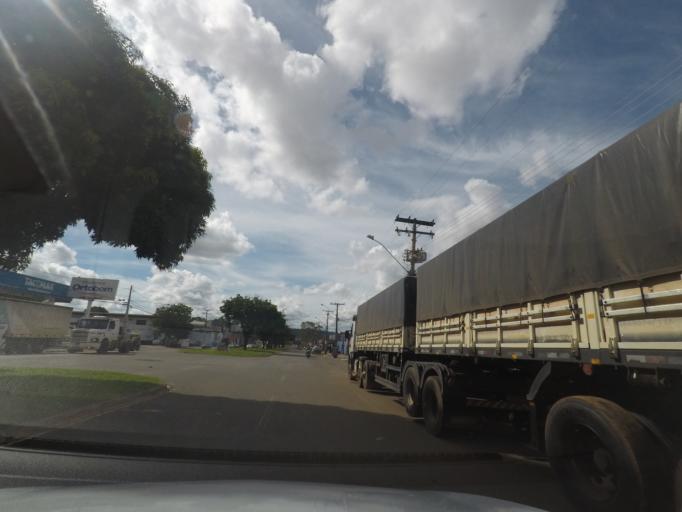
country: BR
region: Goias
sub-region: Goiania
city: Goiania
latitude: -16.6992
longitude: -49.3273
